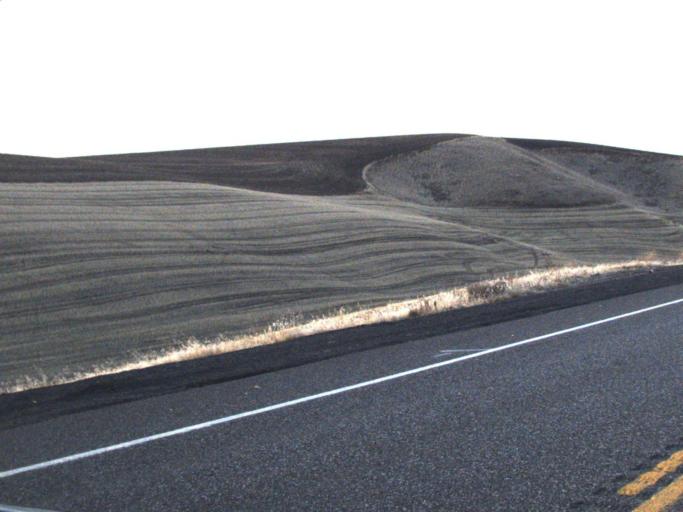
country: US
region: Washington
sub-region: Garfield County
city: Pomeroy
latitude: 46.7262
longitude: -117.7639
